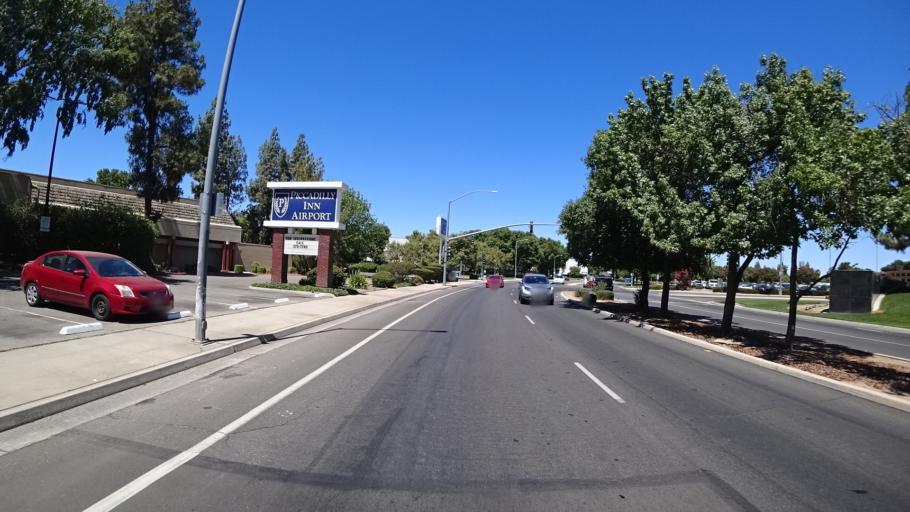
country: US
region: California
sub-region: Fresno County
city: Sunnyside
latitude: 36.7668
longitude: -119.7203
